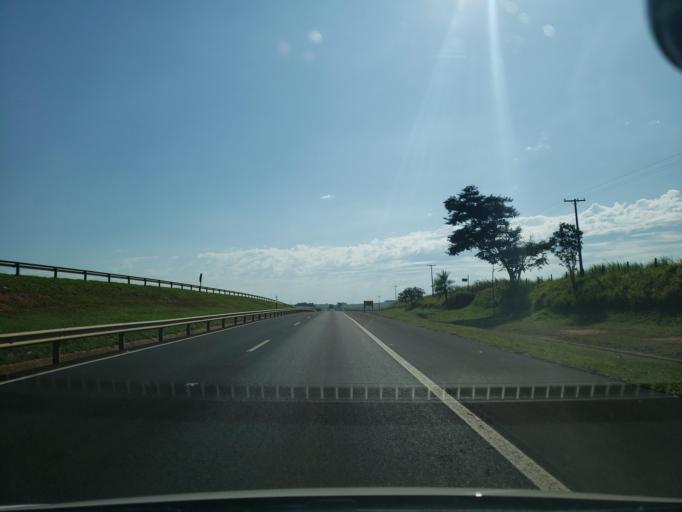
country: BR
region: Sao Paulo
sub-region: Promissao
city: Promissao
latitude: -21.5323
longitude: -49.9826
